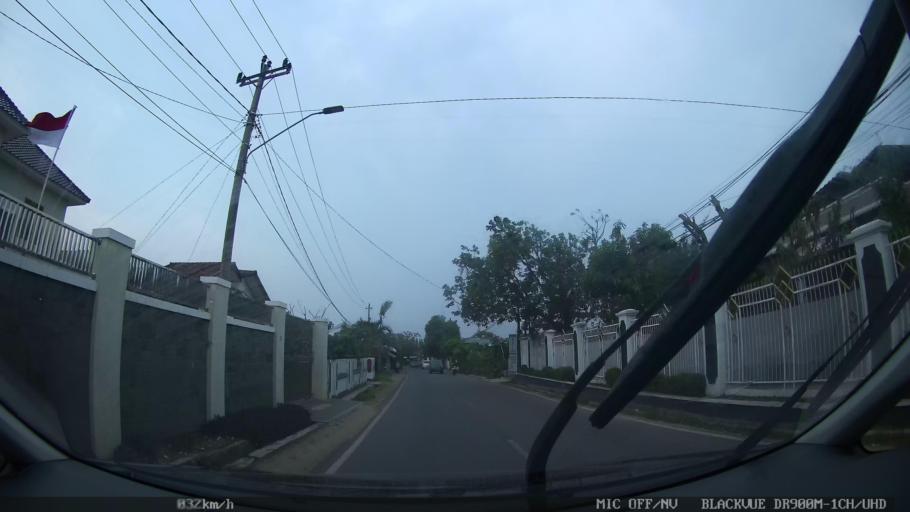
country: ID
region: Lampung
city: Kedaton
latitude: -5.3933
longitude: 105.2787
